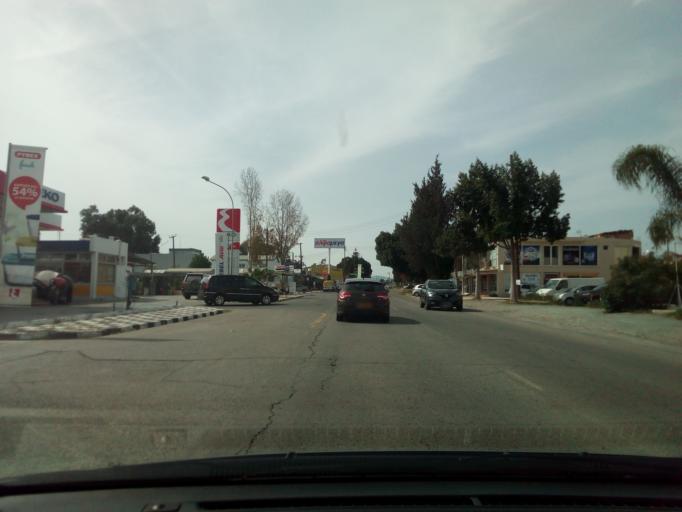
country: CY
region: Lefkosia
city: Kato Deftera
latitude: 35.0892
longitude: 33.2858
